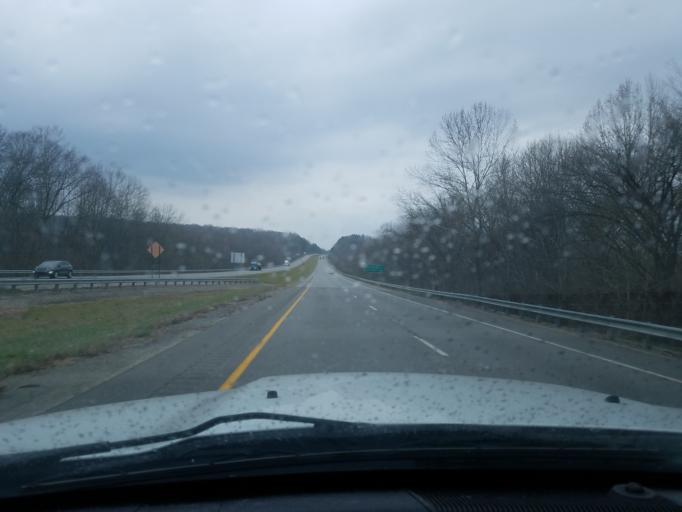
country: US
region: Kentucky
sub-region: Rowan County
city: Morehead
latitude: 38.1877
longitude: -83.4956
